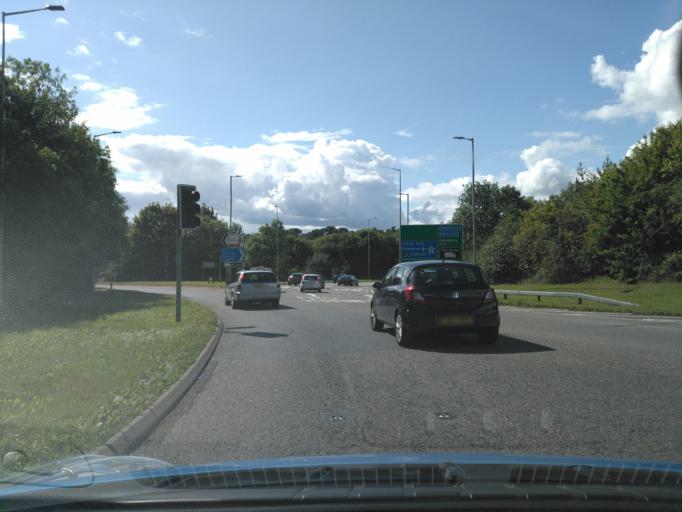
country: GB
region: England
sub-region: Hertfordshire
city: Abbots Langley
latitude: 51.6839
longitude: -0.4294
